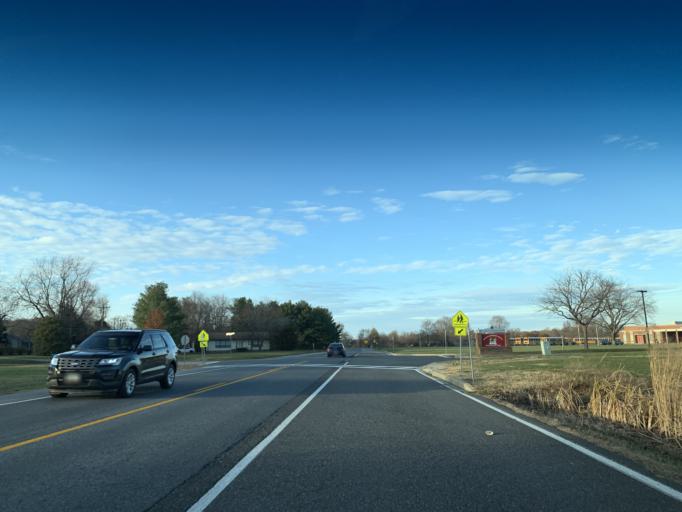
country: US
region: Maryland
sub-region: Kent County
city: Chestertown
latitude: 39.2818
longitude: -76.0944
